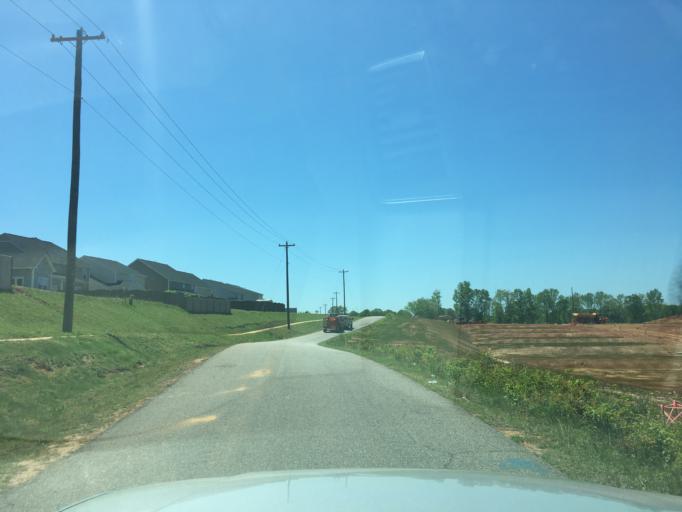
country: US
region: South Carolina
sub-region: Spartanburg County
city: Duncan
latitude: 34.8625
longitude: -82.1506
